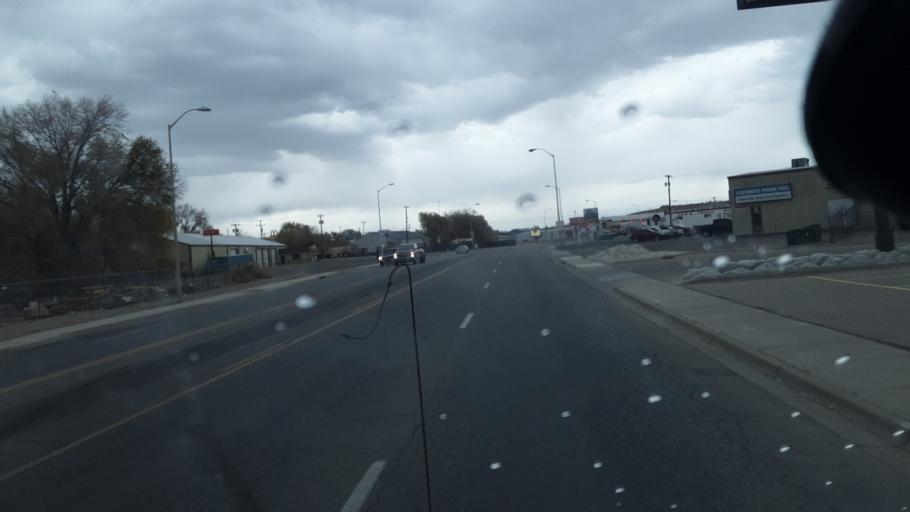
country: US
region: New Mexico
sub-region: San Juan County
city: Farmington
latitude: 36.7364
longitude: -108.1804
